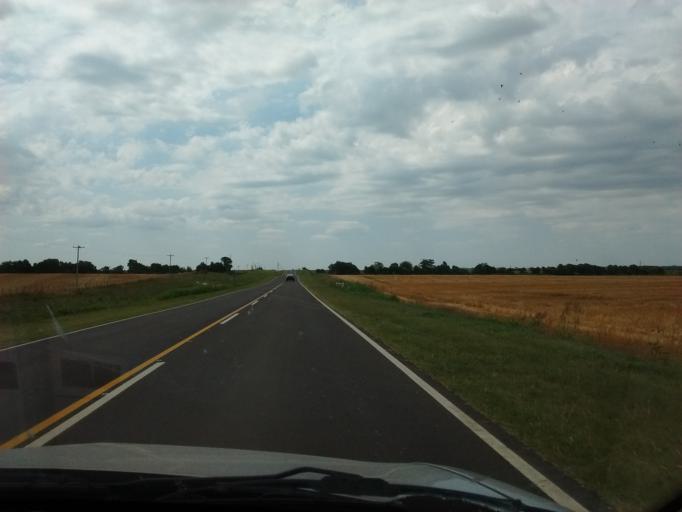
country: AR
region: Entre Rios
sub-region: Departamento de Victoria
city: Victoria
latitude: -32.7927
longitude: -59.8984
